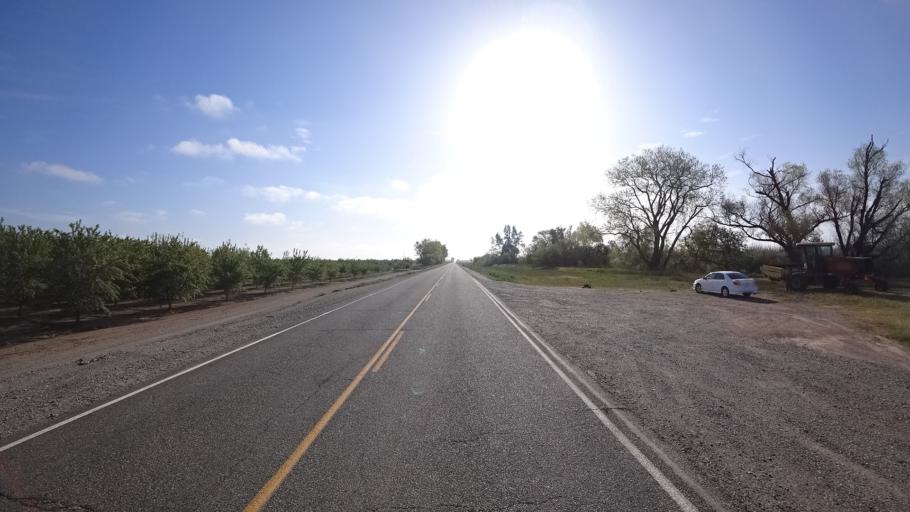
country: US
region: California
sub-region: Glenn County
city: Willows
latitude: 39.5823
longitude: -122.1807
